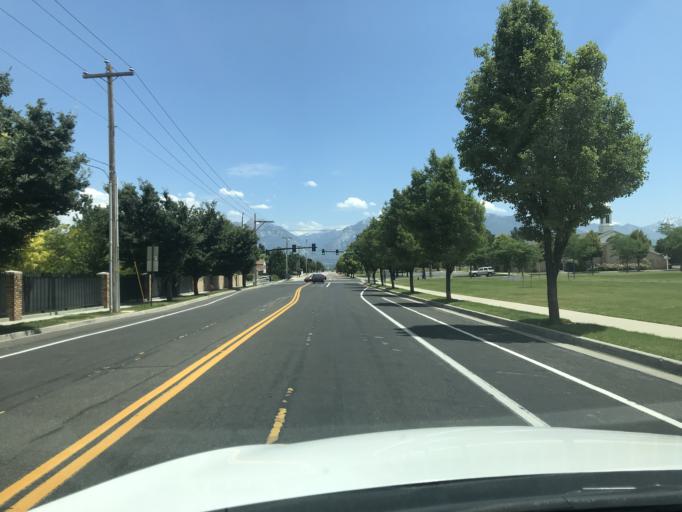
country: US
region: Utah
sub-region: Salt Lake County
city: South Jordan Heights
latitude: 40.5660
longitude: -111.9876
